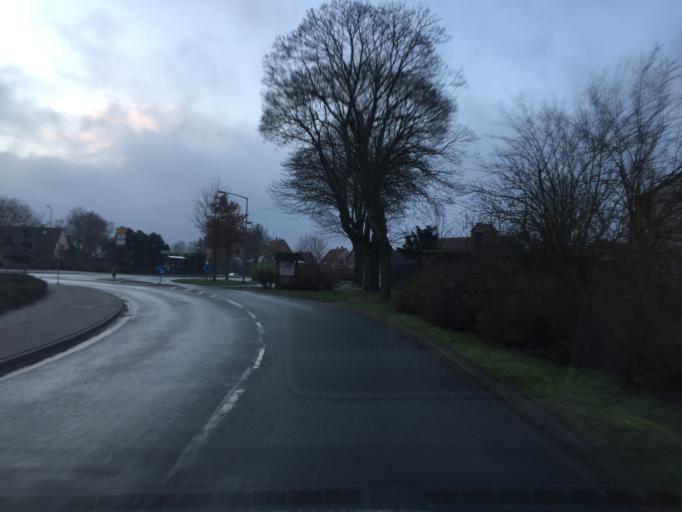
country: DE
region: Lower Saxony
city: Liebenau
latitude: 52.6088
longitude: 9.0870
